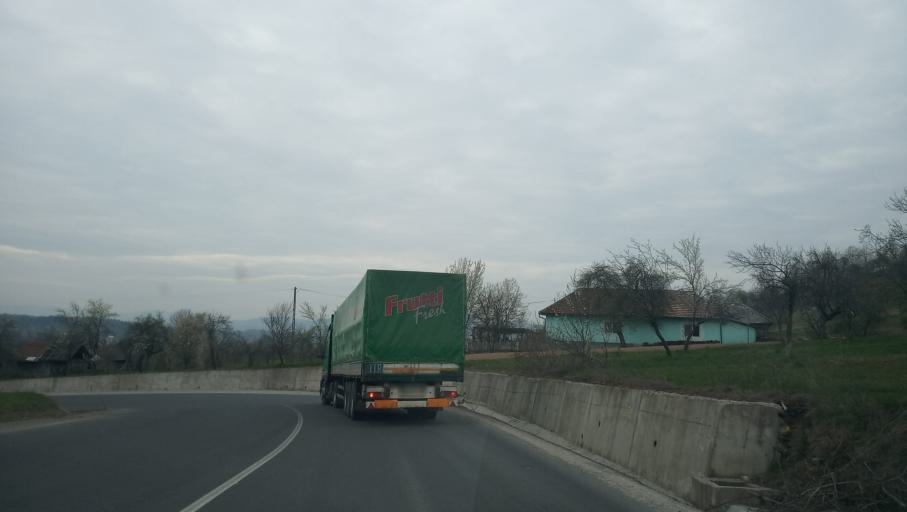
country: RO
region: Arad
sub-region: Comuna Varfurile
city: Varfurile
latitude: 46.3433
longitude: 22.5536
